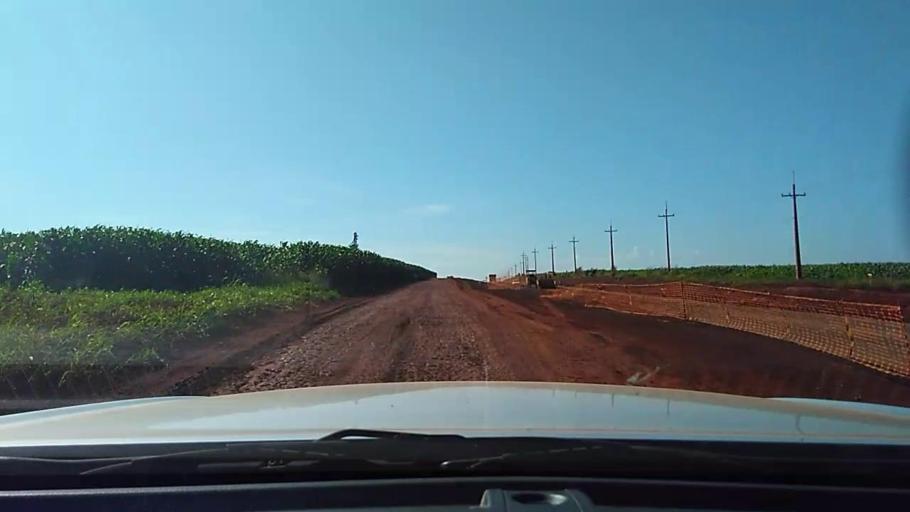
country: PY
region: Alto Parana
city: Naranjal
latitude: -25.9203
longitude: -55.4181
